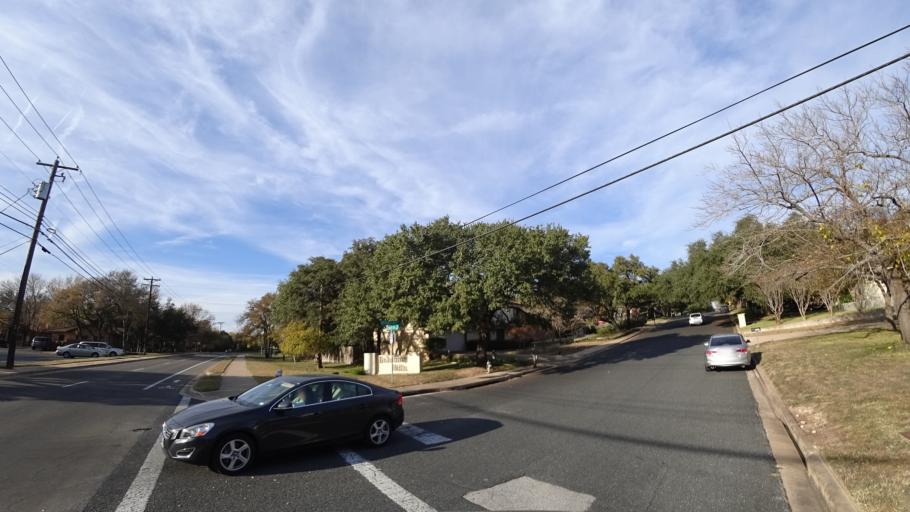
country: US
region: Texas
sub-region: Williamson County
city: Jollyville
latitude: 30.3674
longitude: -97.7527
